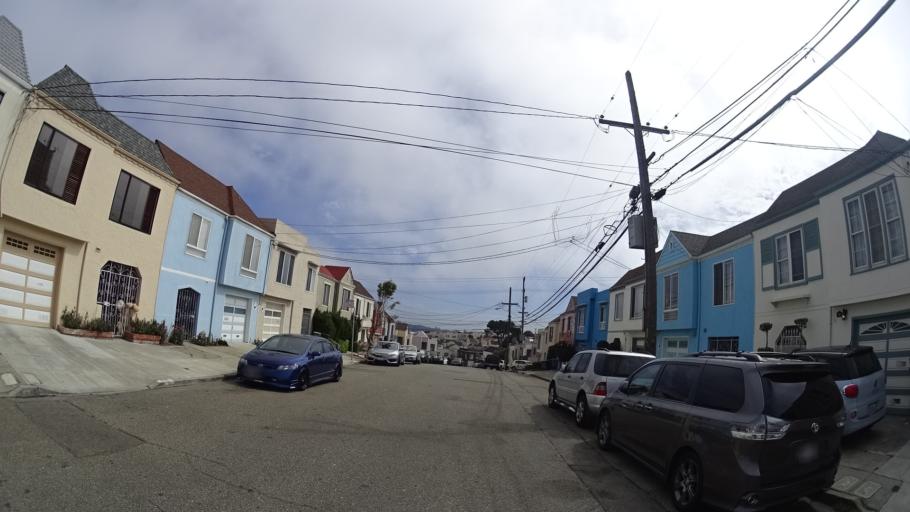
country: US
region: California
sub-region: San Francisco County
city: San Francisco
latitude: 37.7303
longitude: -122.4180
